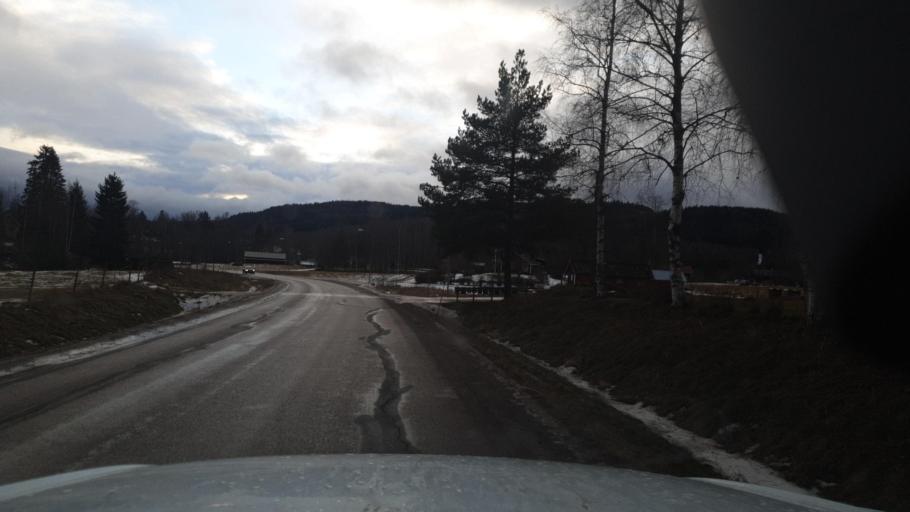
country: SE
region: Vaermland
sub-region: Arvika Kommun
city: Arvika
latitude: 59.7464
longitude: 12.8139
